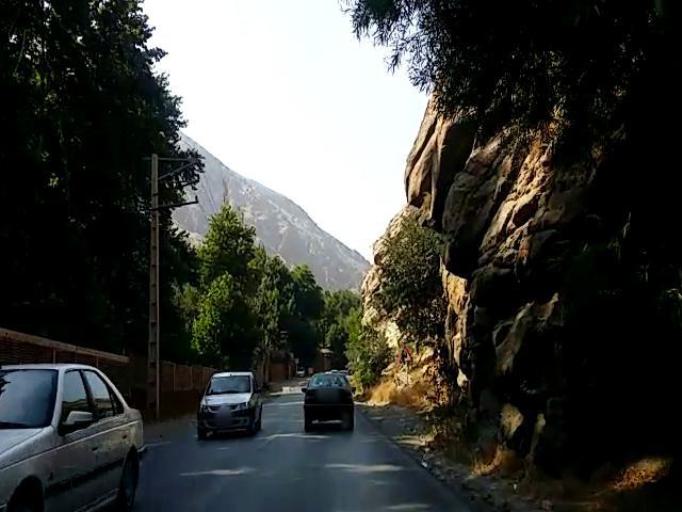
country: IR
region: Alborz
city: Karaj
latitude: 35.8967
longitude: 51.0452
